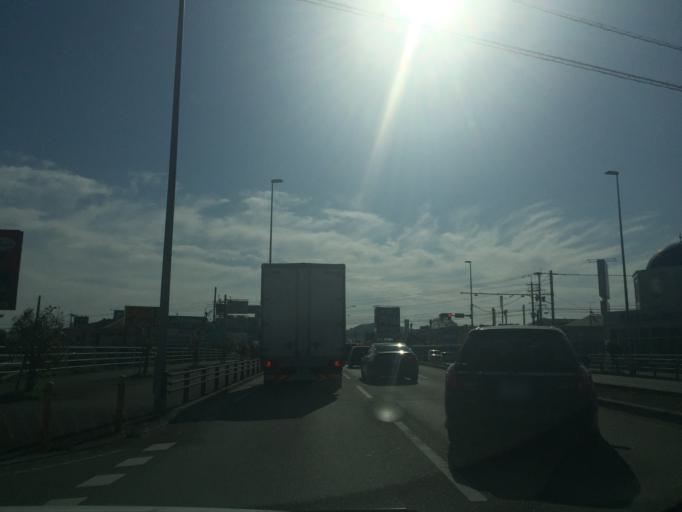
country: JP
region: Fukuoka
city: Umi
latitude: 33.5935
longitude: 130.4769
